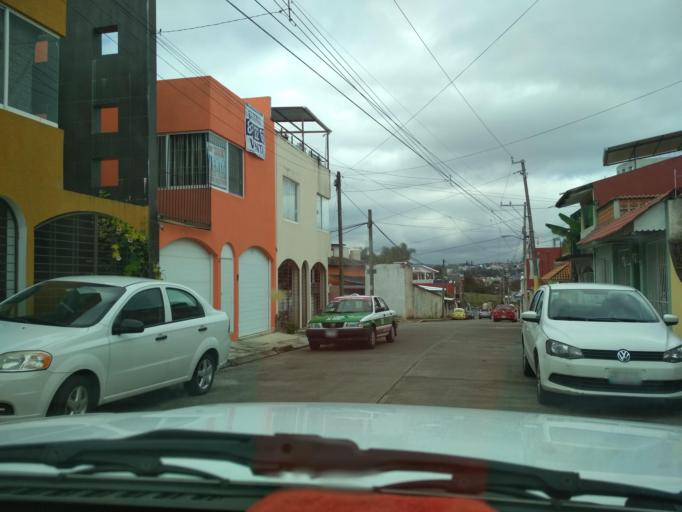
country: MX
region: Veracruz
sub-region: Xalapa
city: Xalapa de Enriquez
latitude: 19.5084
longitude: -96.9260
